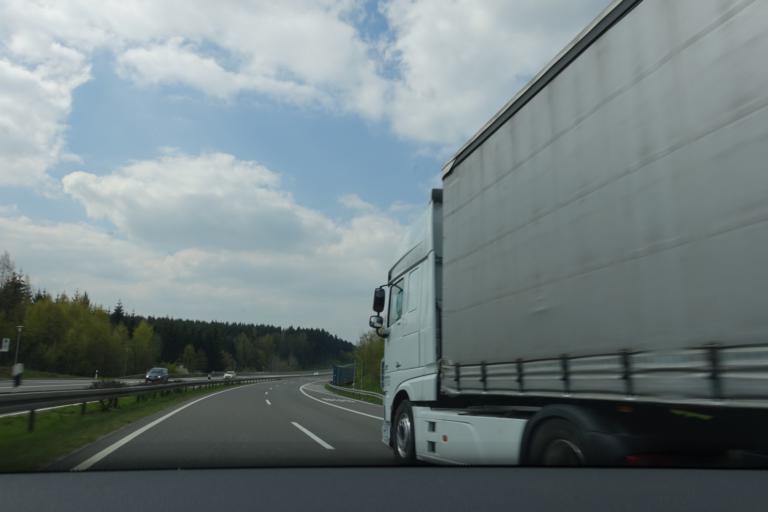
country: DE
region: Saxony
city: Gornau
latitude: 50.7705
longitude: 13.0125
